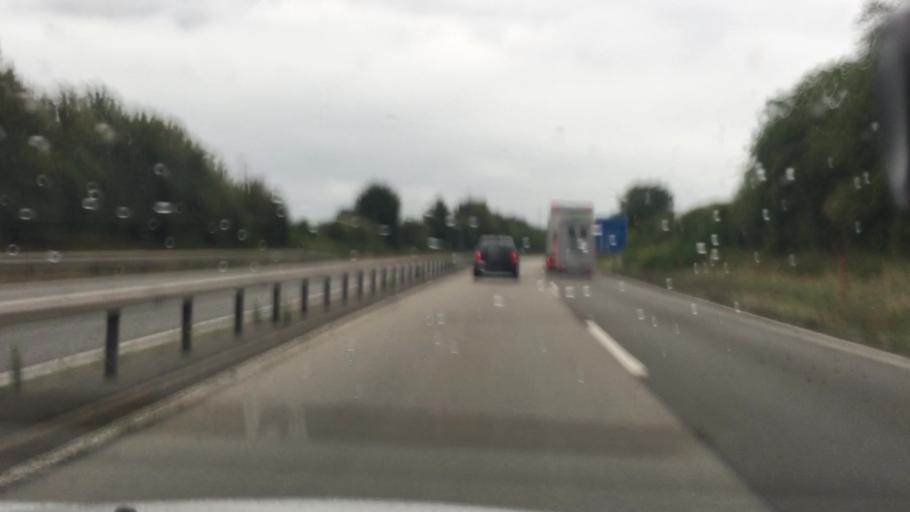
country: DE
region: Rheinland-Pfalz
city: Insheim
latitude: 49.1626
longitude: 8.1549
